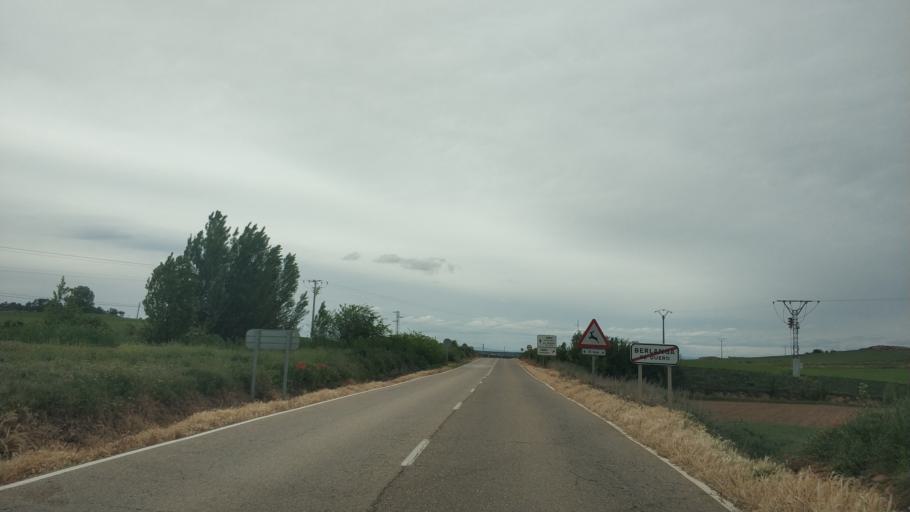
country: ES
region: Castille and Leon
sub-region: Provincia de Soria
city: Berlanga de Duero
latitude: 41.4724
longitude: -2.8614
